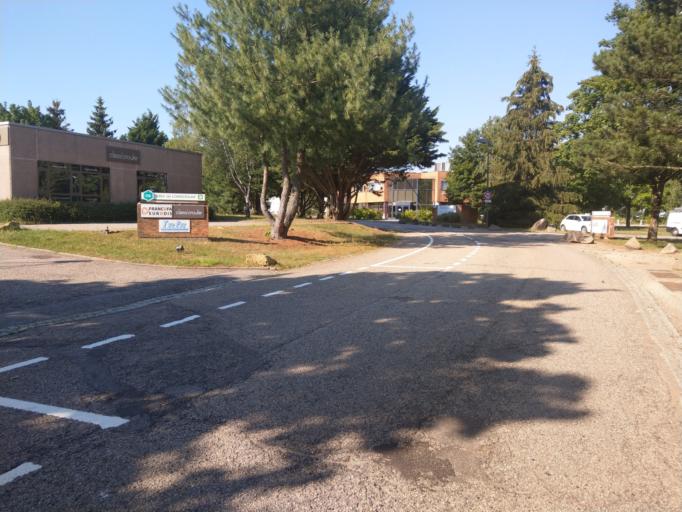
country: FR
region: Lorraine
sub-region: Departement de Meurthe-et-Moselle
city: Villers-les-Nancy
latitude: 48.6542
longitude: 6.1373
